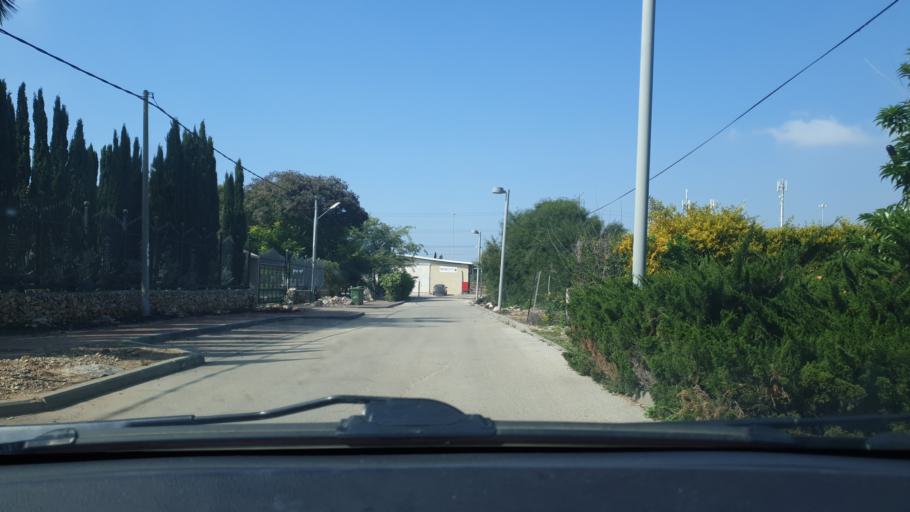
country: IL
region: Central District
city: Bet Dagan
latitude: 32.0098
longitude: 34.8182
